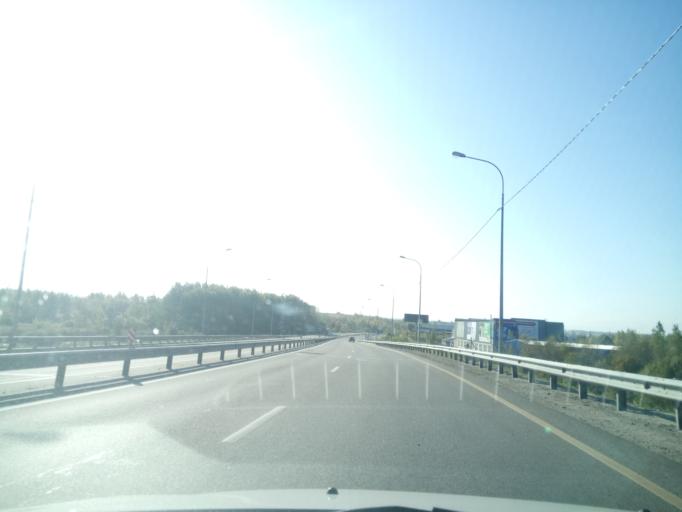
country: RU
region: Nizjnij Novgorod
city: Burevestnik
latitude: 56.1758
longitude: 43.9135
